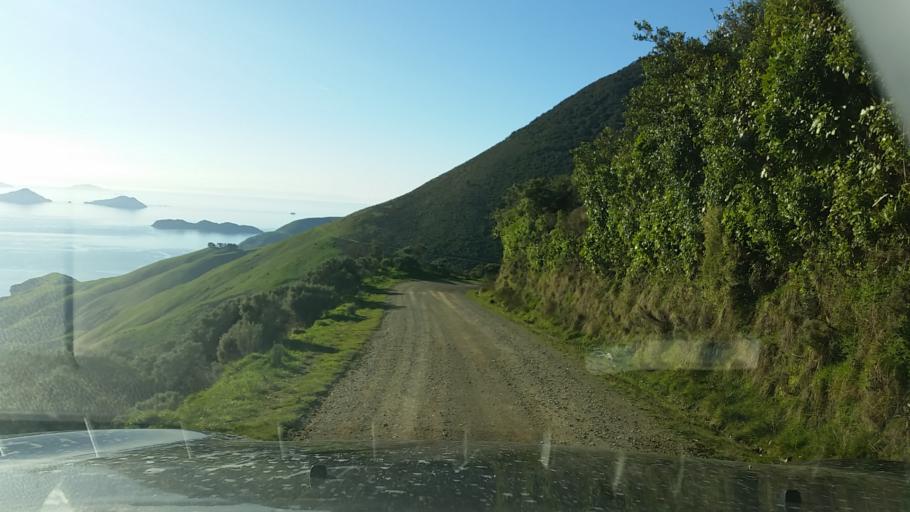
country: NZ
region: Marlborough
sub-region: Marlborough District
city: Picton
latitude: -41.0264
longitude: 174.1586
